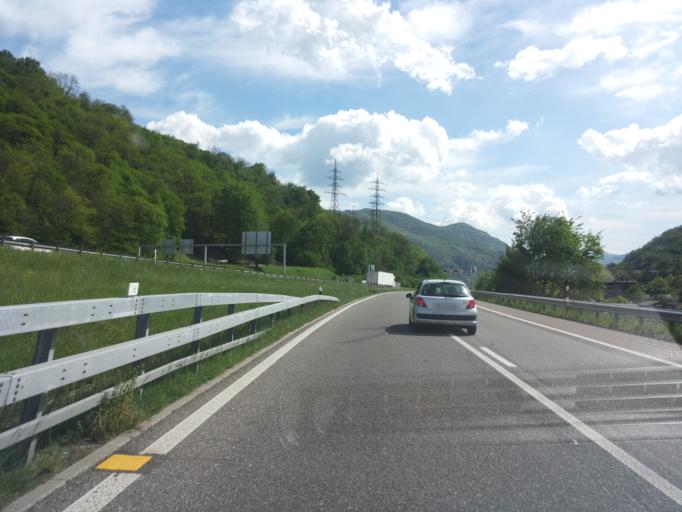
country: CH
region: Ticino
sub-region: Lugano District
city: Montagnola
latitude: 45.9819
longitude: 8.9323
